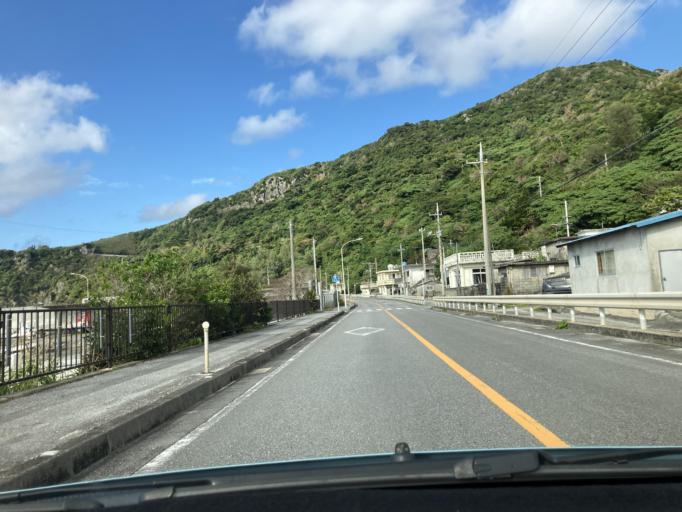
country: JP
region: Okinawa
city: Nago
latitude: 26.8482
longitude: 128.2538
